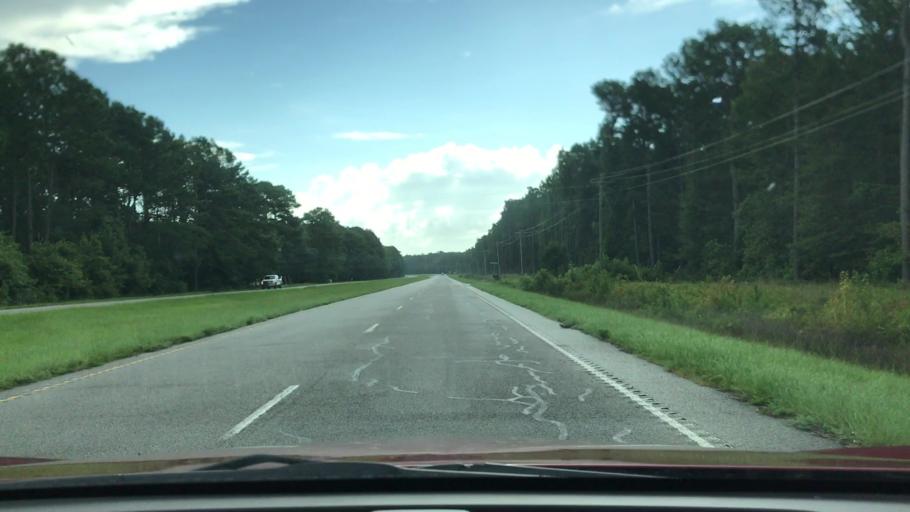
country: US
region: South Carolina
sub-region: Charleston County
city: Awendaw
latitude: 33.0458
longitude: -79.5745
